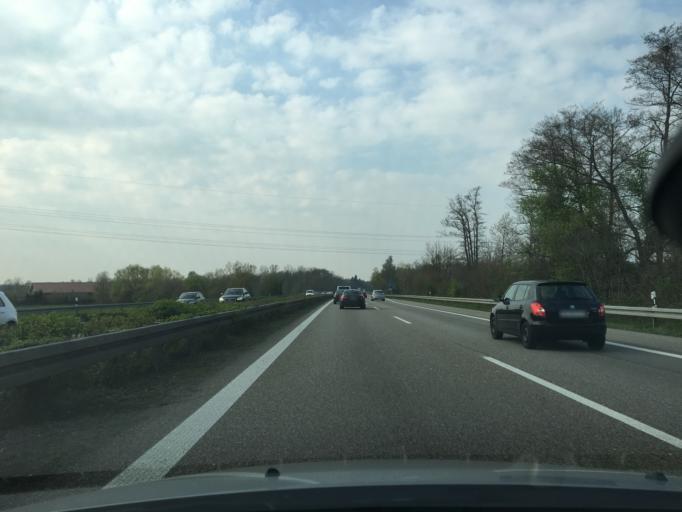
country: DE
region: Baden-Wuerttemberg
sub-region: Freiburg Region
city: Teningen
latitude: 48.0897
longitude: 7.7971
